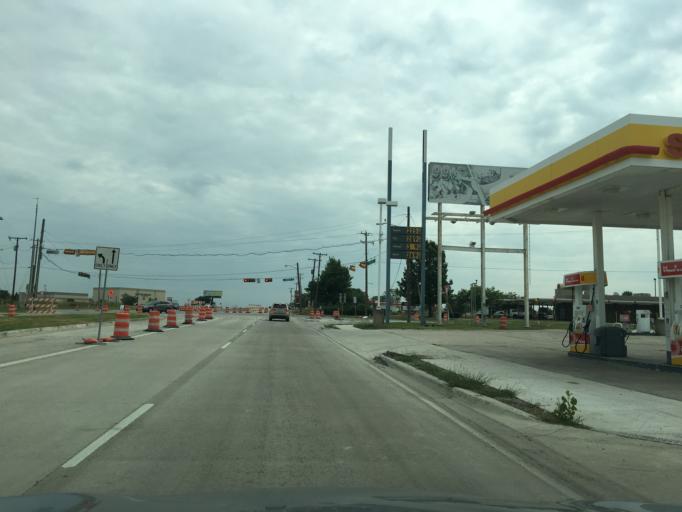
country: US
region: Texas
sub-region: Collin County
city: Melissa
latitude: 33.2784
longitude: -96.5696
